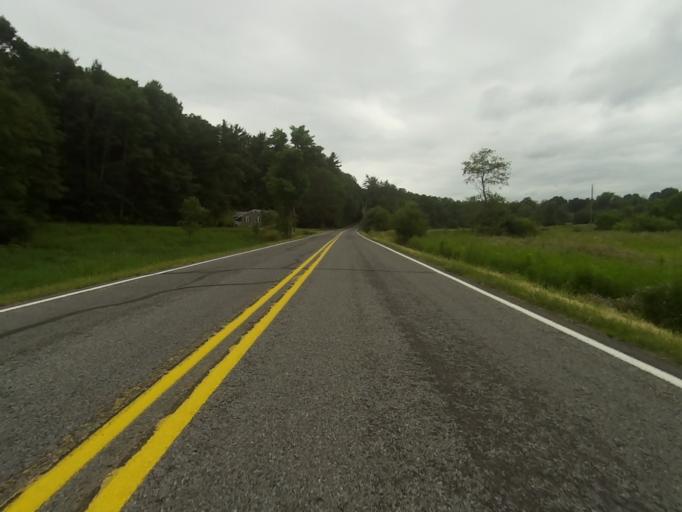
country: US
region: Pennsylvania
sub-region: Centre County
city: Stormstown
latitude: 40.7247
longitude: -77.9864
